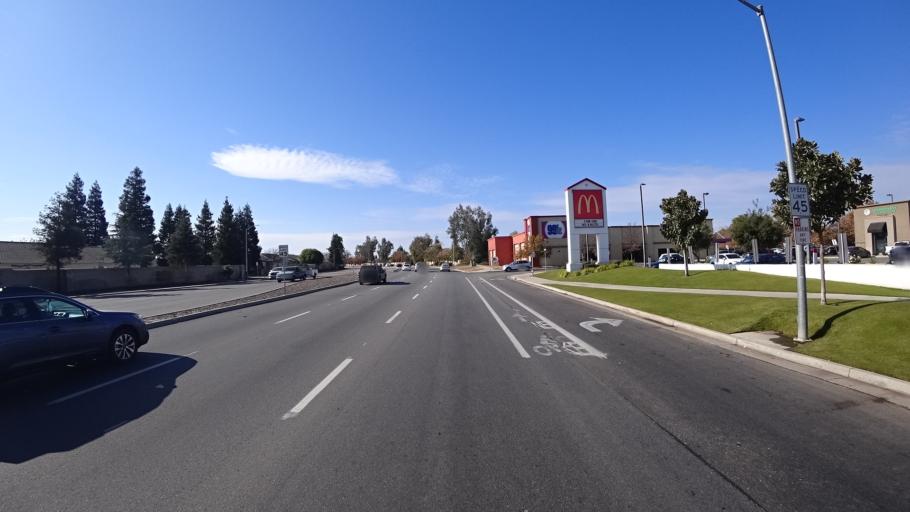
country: US
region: California
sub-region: Kern County
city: Greenacres
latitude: 35.4017
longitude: -119.0931
